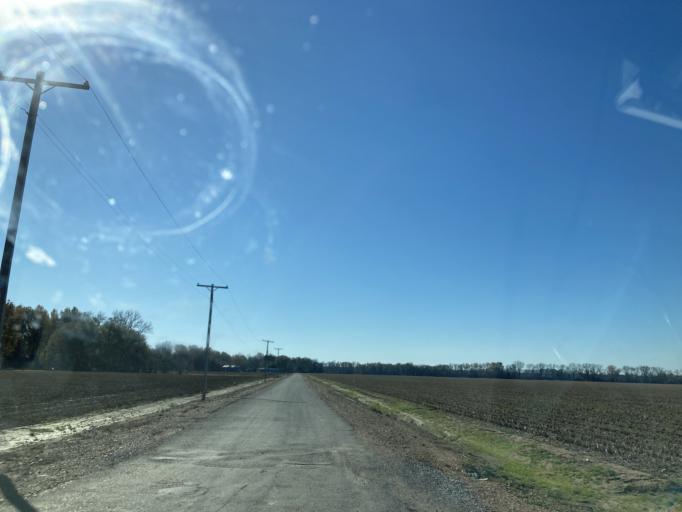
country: US
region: Mississippi
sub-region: Sharkey County
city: Rolling Fork
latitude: 32.8215
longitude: -90.7291
